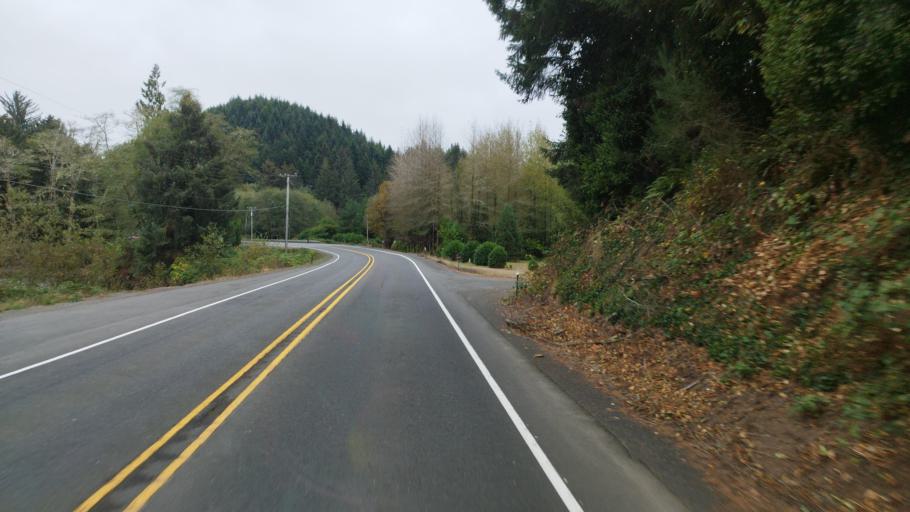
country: US
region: Oregon
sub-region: Clatsop County
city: Cannon Beach
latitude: 45.9211
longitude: -123.8952
